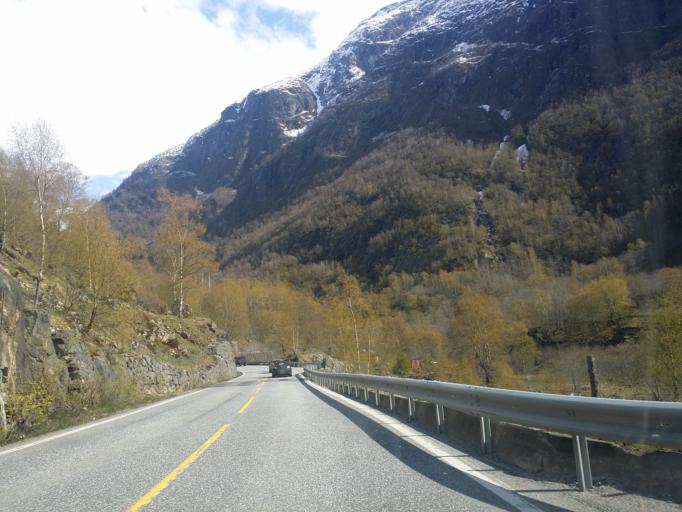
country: NO
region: Hordaland
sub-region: Eidfjord
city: Eidfjord
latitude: 60.4173
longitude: 7.1452
